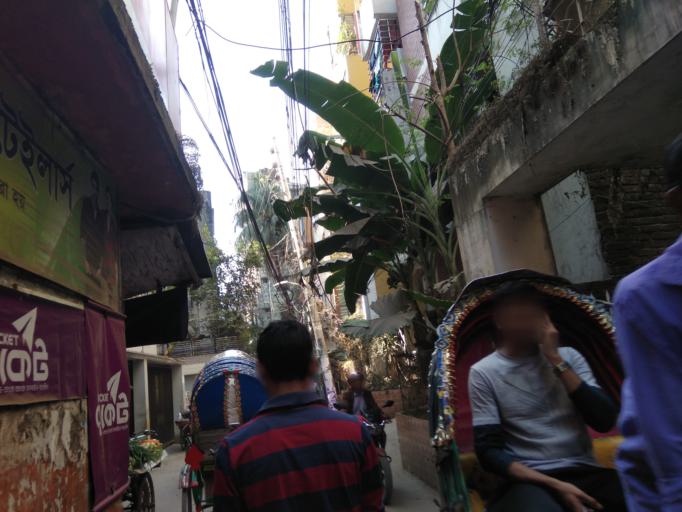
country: BD
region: Dhaka
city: Azimpur
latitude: 23.7395
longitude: 90.3728
